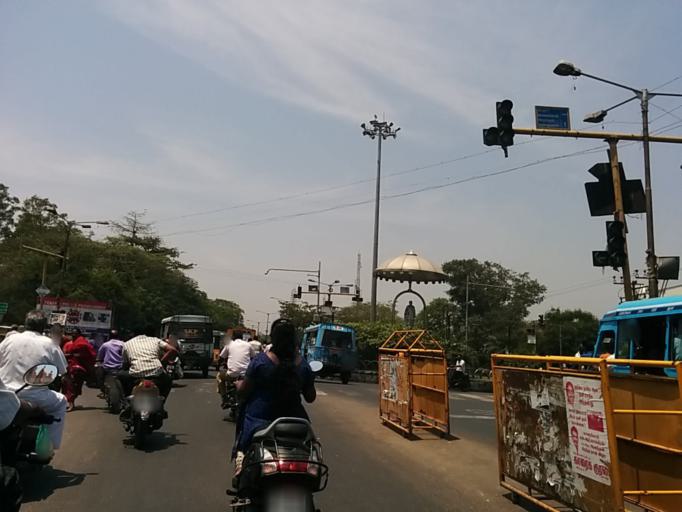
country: IN
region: Pondicherry
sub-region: Puducherry
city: Puducherry
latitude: 11.9309
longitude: 79.8209
